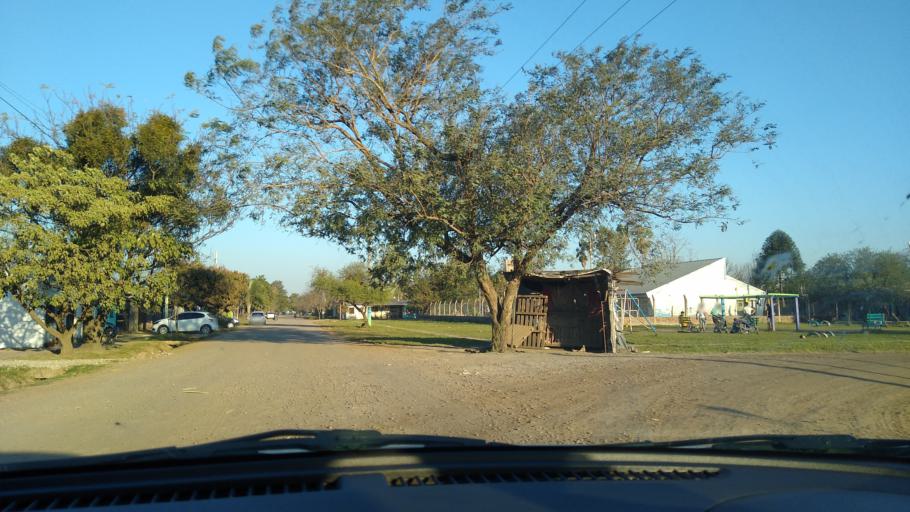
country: AR
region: Chaco
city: Resistencia
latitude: -27.4855
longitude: -58.9791
